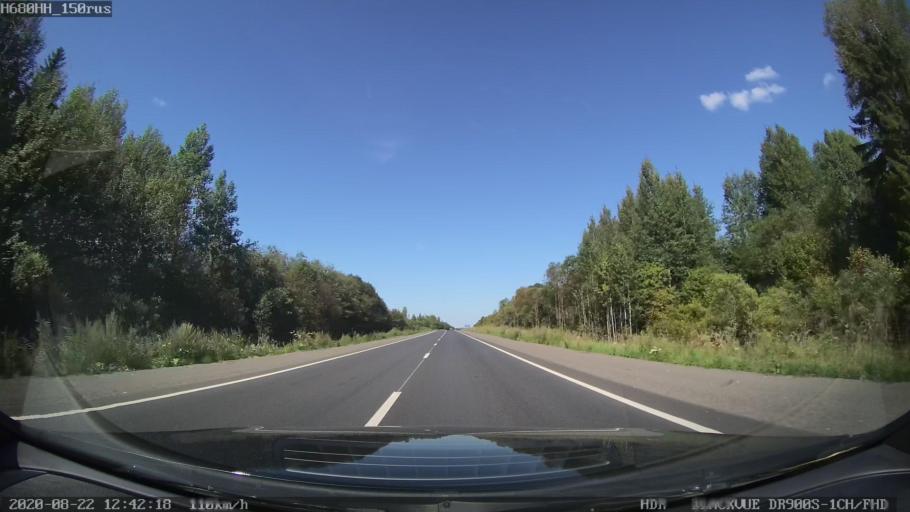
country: RU
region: Tverskaya
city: Rameshki
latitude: 57.3599
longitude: 36.0944
